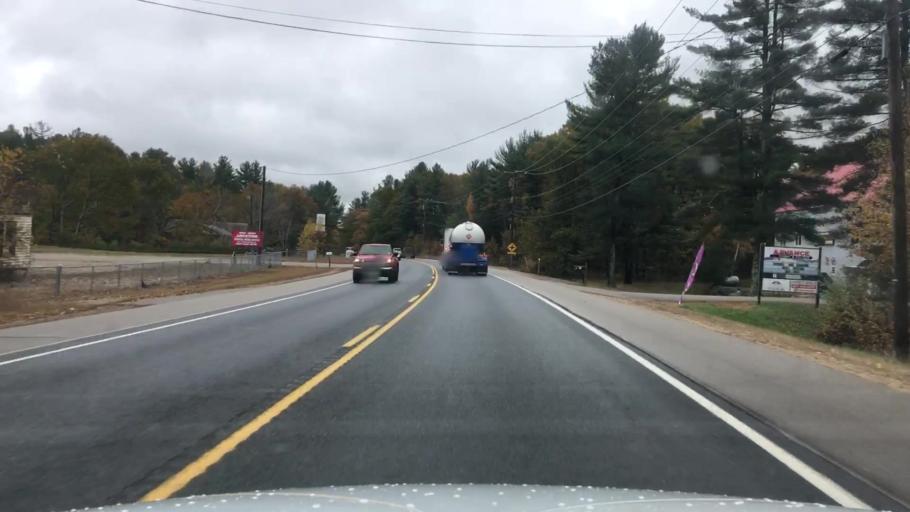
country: US
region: New Hampshire
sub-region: Strafford County
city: Lee
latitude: 43.1614
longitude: -71.0061
